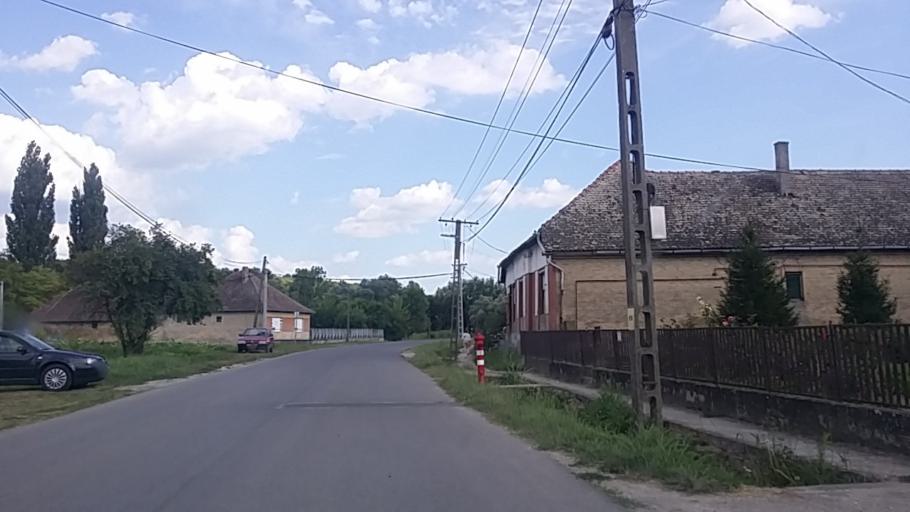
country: HU
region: Tolna
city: Gyonk
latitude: 46.5270
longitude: 18.5142
